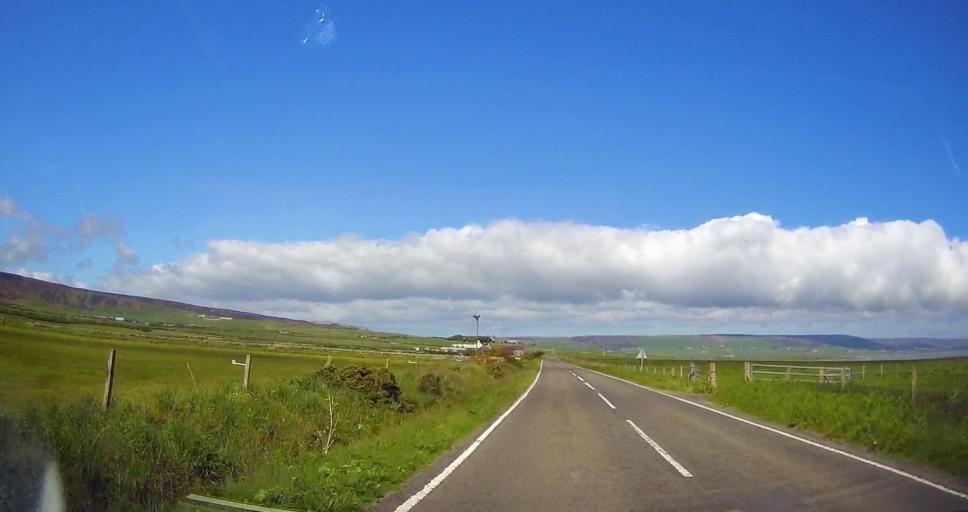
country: GB
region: Scotland
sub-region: Orkney Islands
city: Orkney
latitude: 58.9893
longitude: -3.0648
